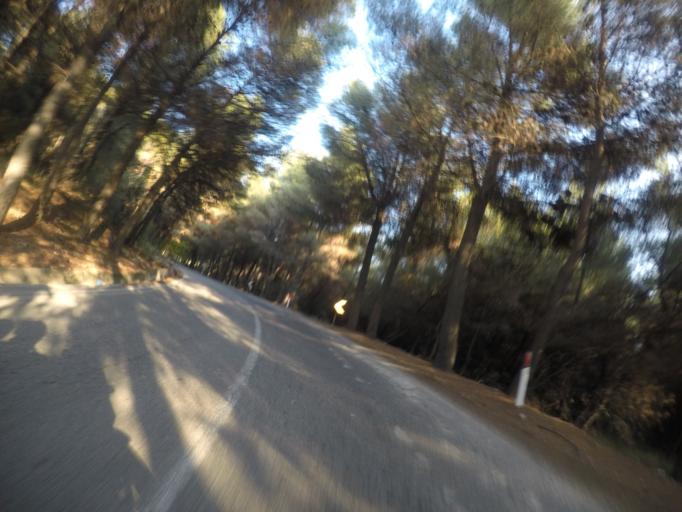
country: AL
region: Durres
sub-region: Rrethi i Krujes
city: Kruje
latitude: 41.4918
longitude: 19.7674
